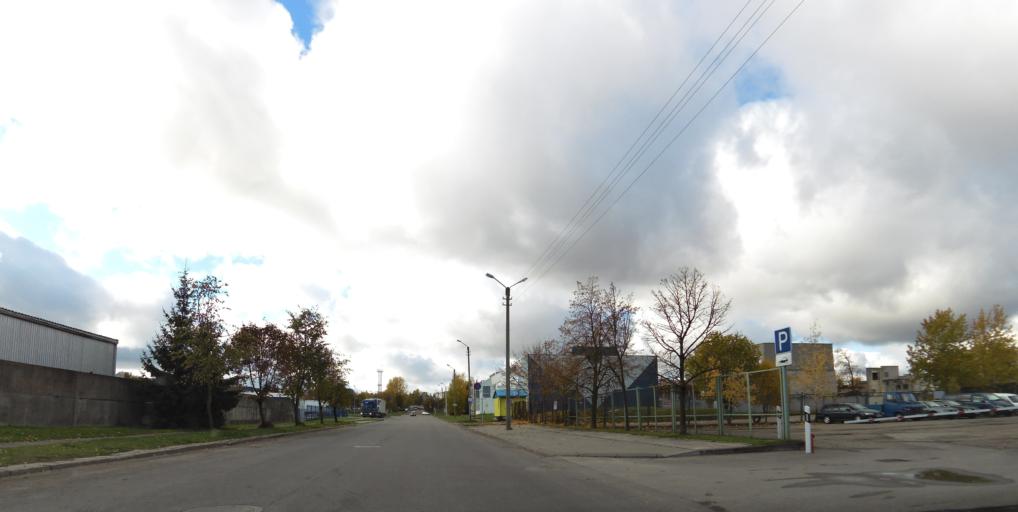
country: LT
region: Vilnius County
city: Vilkpede
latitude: 54.6410
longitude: 25.2698
